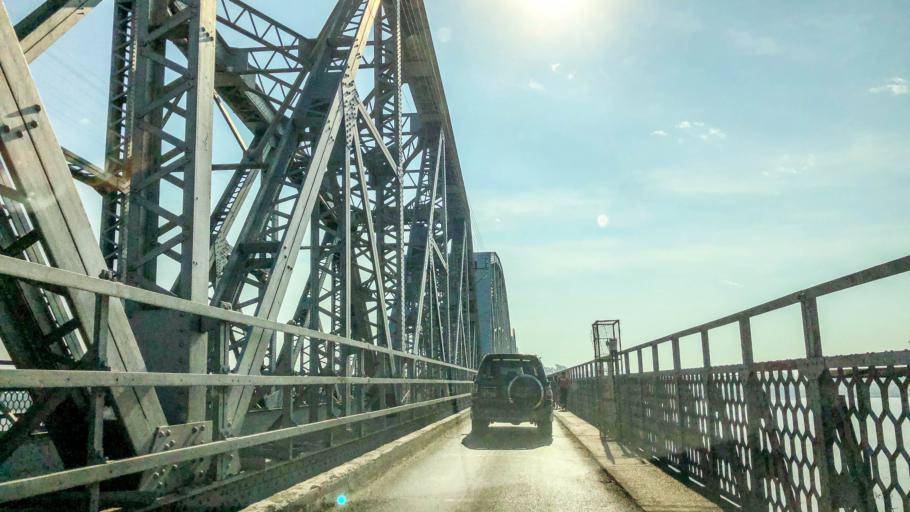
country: MM
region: Sagain
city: Sagaing
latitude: 21.8744
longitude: 95.9886
